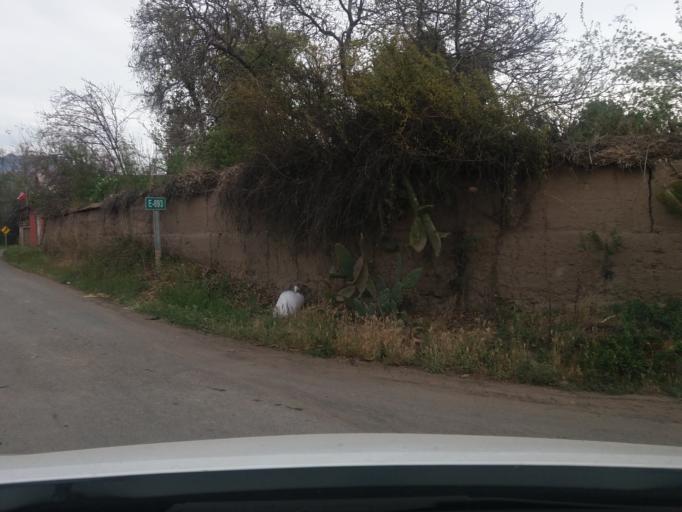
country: CL
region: Valparaiso
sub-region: Provincia de Los Andes
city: Los Andes
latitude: -32.8534
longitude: -70.6453
